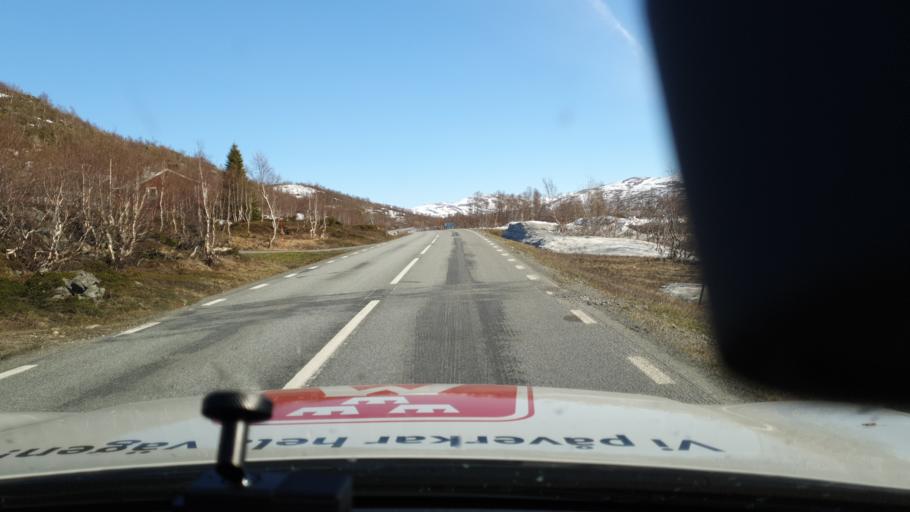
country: NO
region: Nordland
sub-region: Rana
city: Mo i Rana
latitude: 66.1340
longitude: 14.5944
